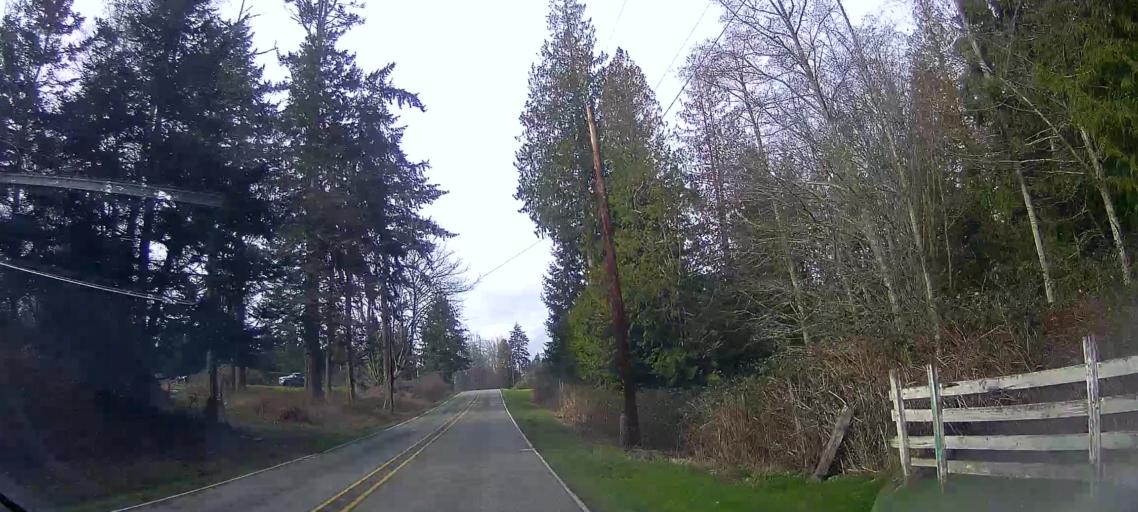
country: US
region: Washington
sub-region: Island County
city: Langley
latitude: 48.0885
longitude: -122.3883
